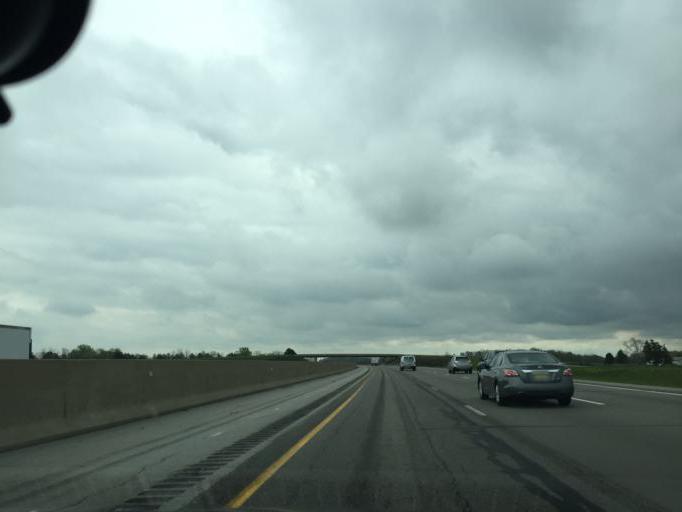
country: US
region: Ohio
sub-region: Sandusky County
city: Clyde
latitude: 41.3633
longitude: -82.9399
